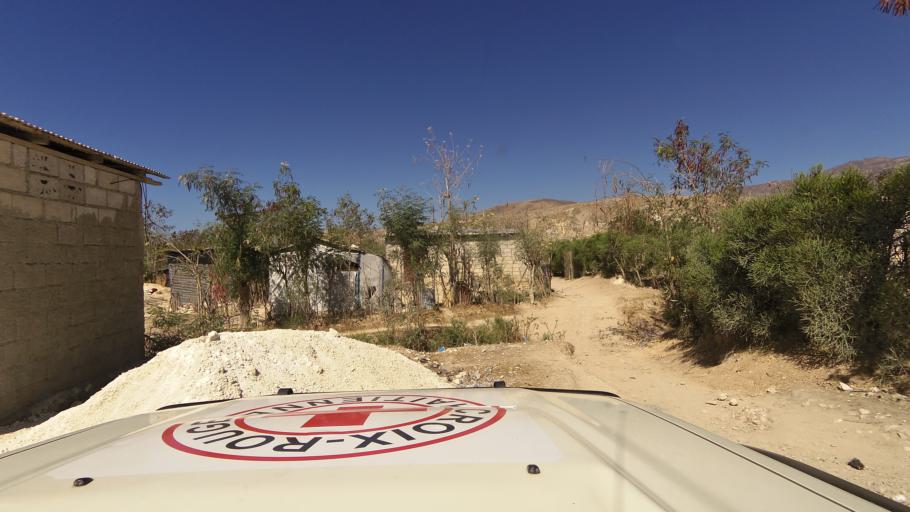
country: HT
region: Ouest
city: Croix des Bouquets
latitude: 18.6587
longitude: -72.2505
